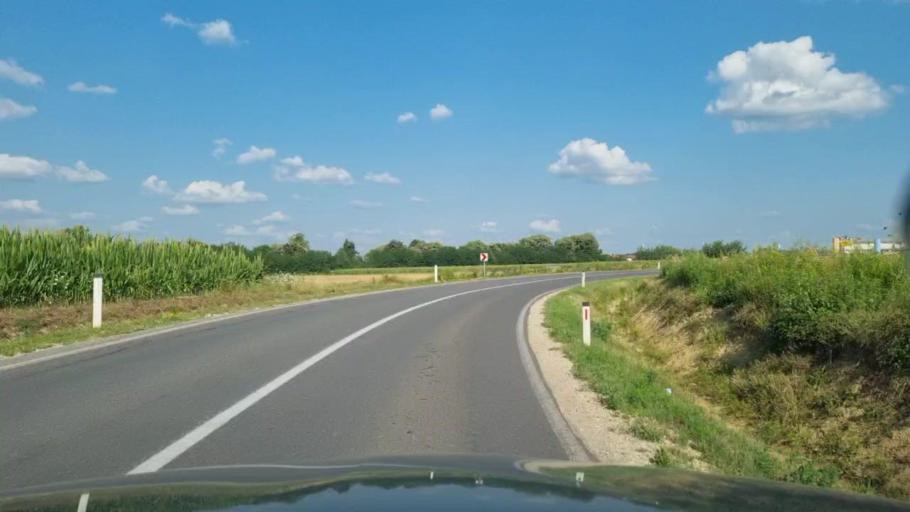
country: BA
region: Federation of Bosnia and Herzegovina
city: Gradacac
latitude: 44.8941
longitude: 18.4004
